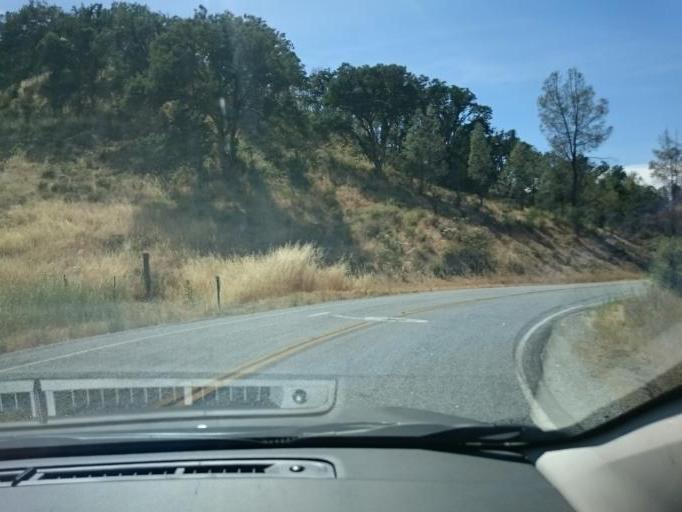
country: US
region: California
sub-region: Santa Clara County
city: Morgan Hill
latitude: 37.3504
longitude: -121.5452
